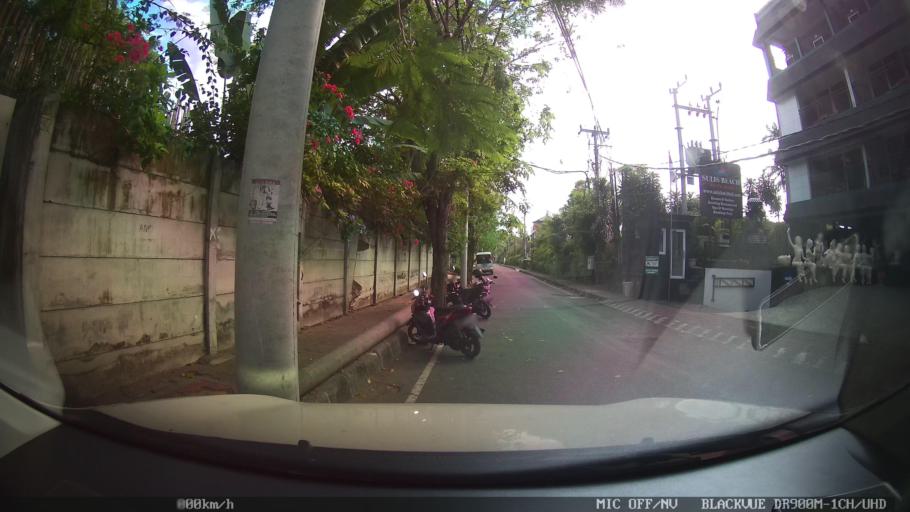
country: ID
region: Bali
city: Jabajero
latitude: -8.7362
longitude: 115.1636
